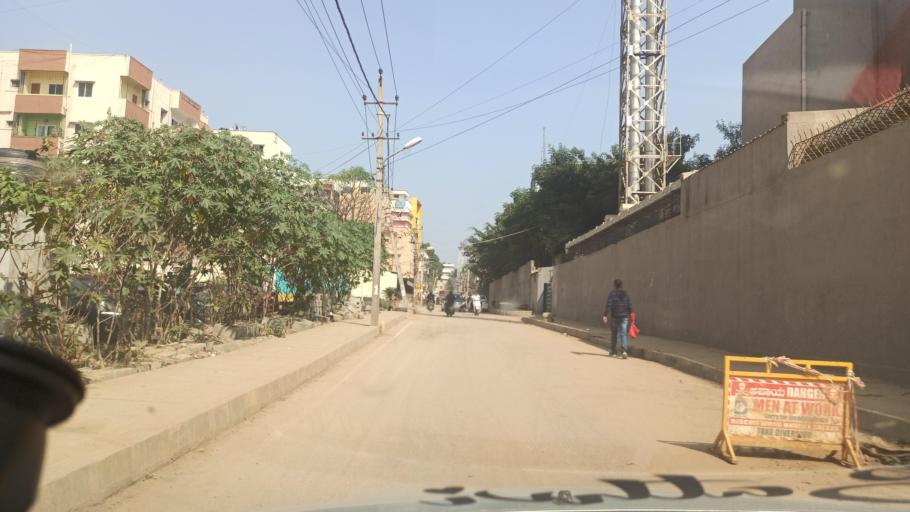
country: IN
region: Karnataka
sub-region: Bangalore Urban
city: Bangalore
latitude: 12.9504
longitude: 77.6978
